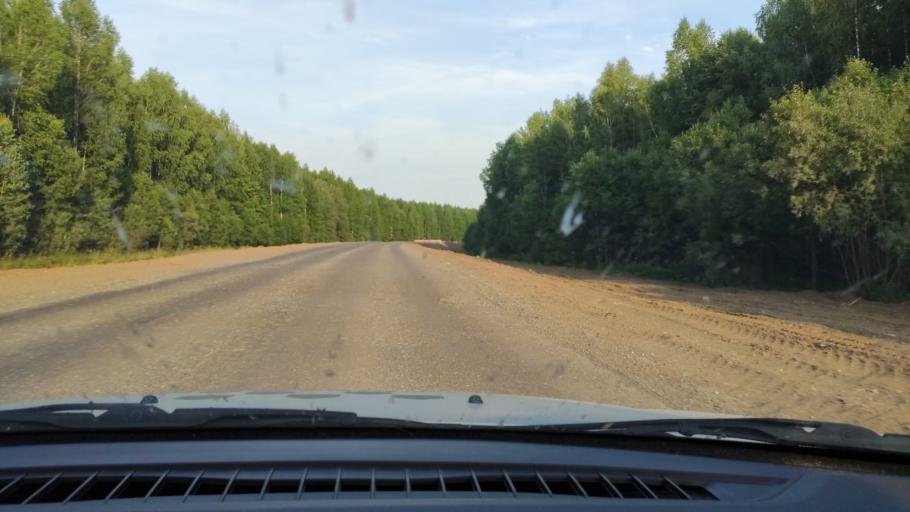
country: RU
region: Perm
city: Siva
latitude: 58.4812
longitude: 54.3934
